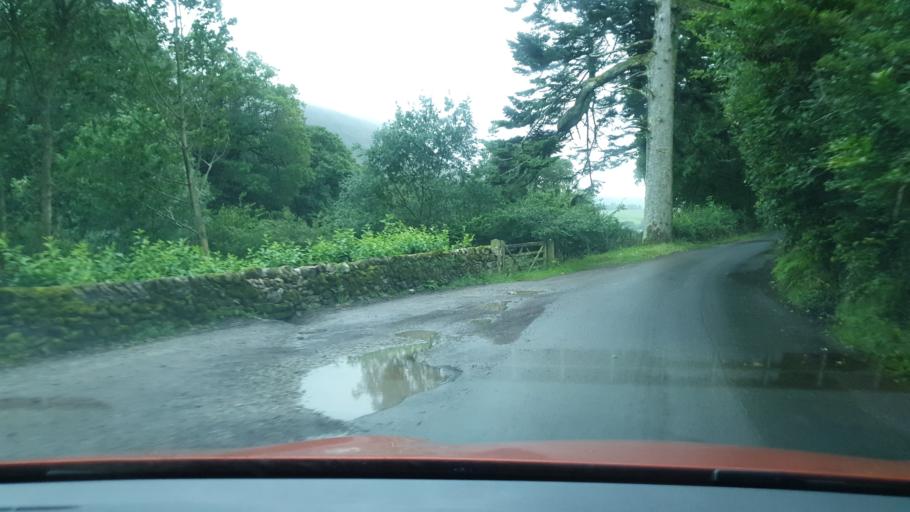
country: GB
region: England
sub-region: Cumbria
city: Seascale
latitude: 54.4273
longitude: -3.3214
